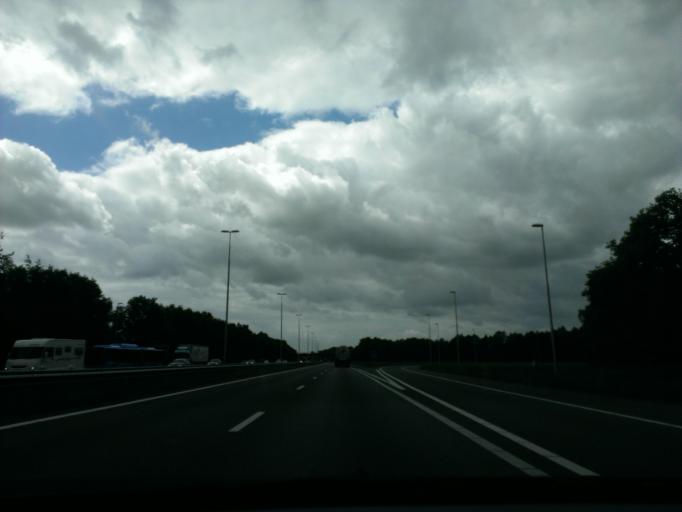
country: NL
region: Gelderland
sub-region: Gemeente Epe
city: Epe
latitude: 52.3337
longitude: 6.0093
